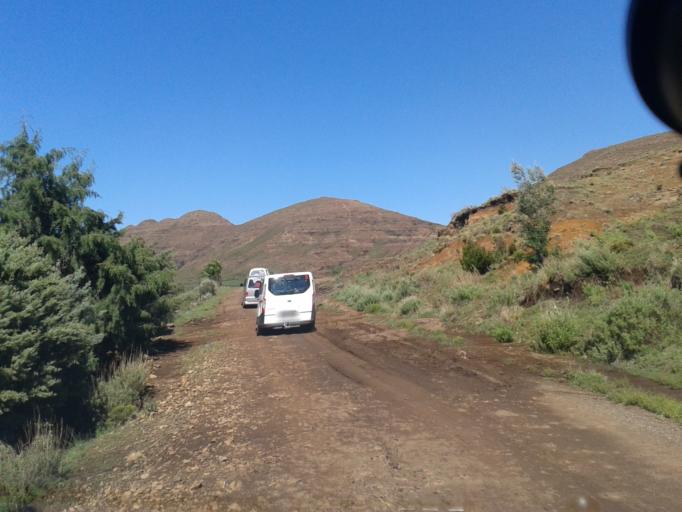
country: LS
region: Maseru
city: Nako
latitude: -29.8456
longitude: 27.5580
